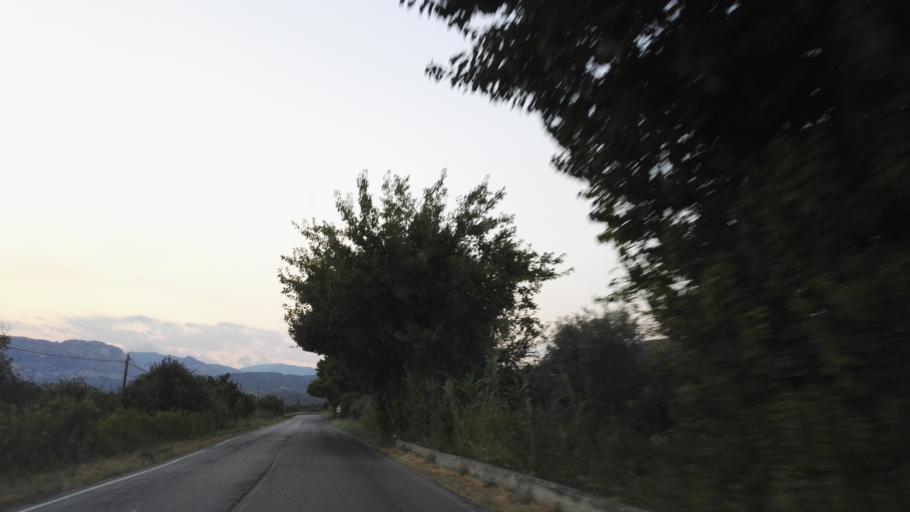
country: IT
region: Calabria
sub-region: Provincia di Reggio Calabria
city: Monasterace
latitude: 38.4480
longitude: 16.5335
